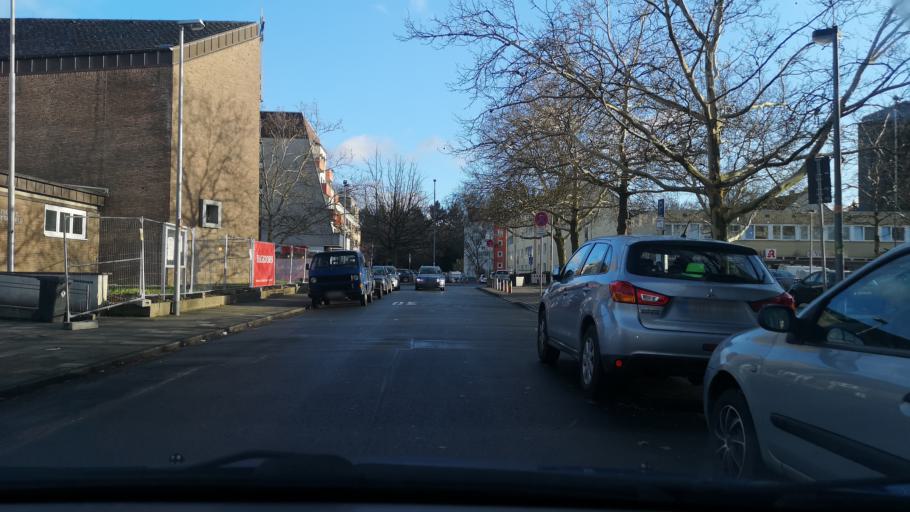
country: DE
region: Lower Saxony
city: Auf der Horst
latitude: 52.4102
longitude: 9.6648
